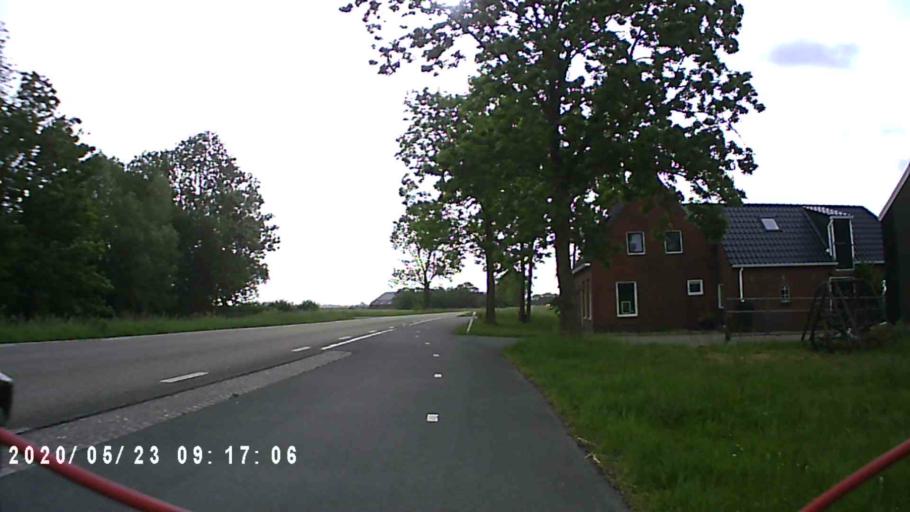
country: NL
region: Groningen
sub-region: Gemeente Bedum
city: Bedum
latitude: 53.3013
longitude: 6.6547
